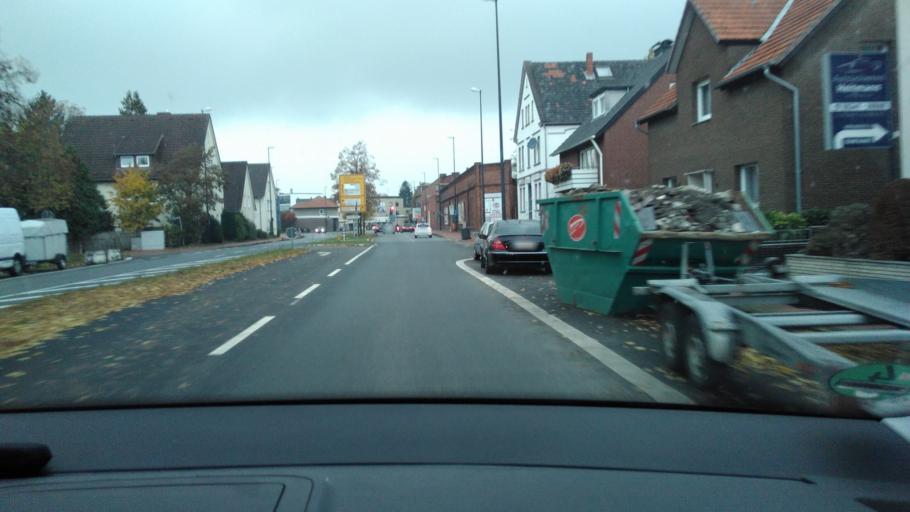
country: DE
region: North Rhine-Westphalia
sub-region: Regierungsbezirk Detmold
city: Guetersloh
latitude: 51.9032
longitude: 8.3951
